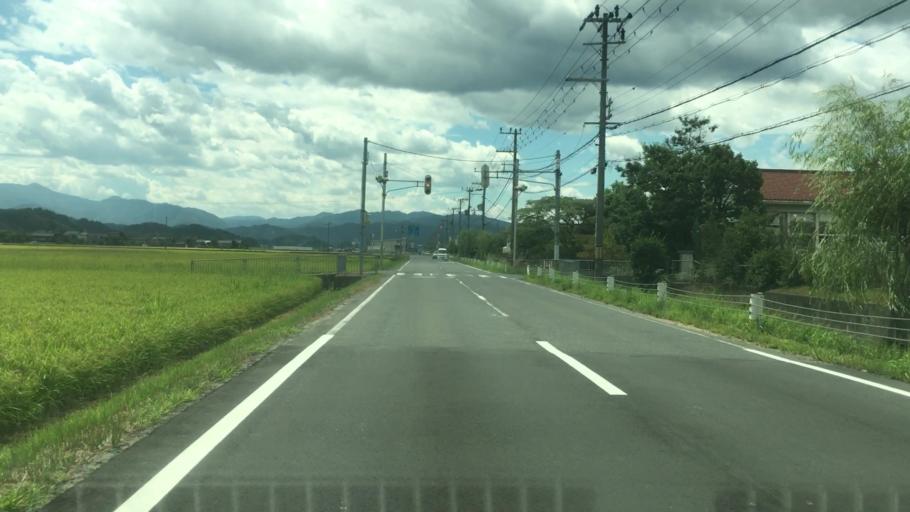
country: JP
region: Hyogo
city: Toyooka
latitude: 35.5303
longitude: 134.8398
